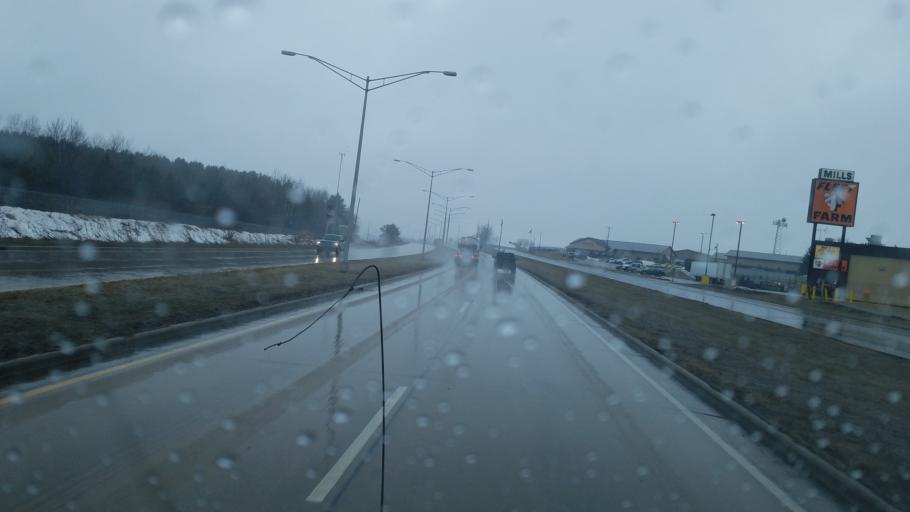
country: US
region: Wisconsin
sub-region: Wood County
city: Marshfield
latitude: 44.6812
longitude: -90.1922
